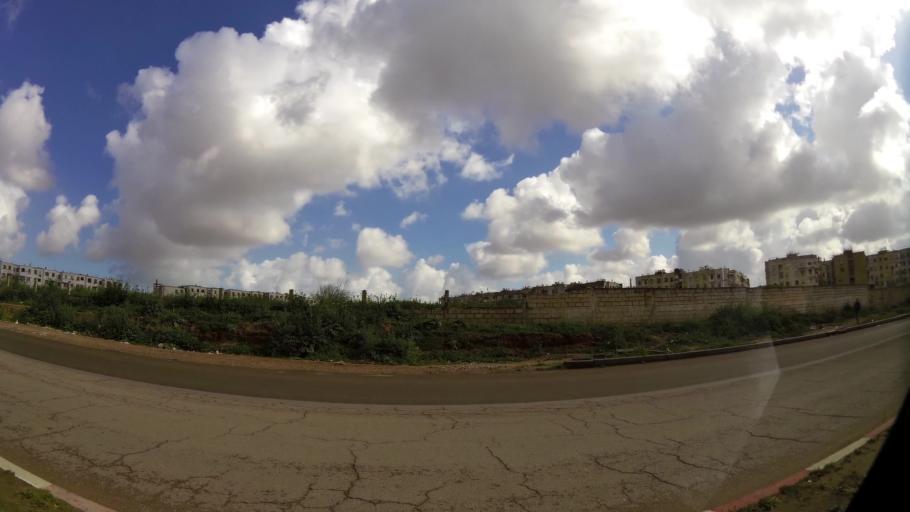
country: MA
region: Grand Casablanca
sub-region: Mediouna
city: Tit Mellil
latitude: 33.5698
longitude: -7.5196
